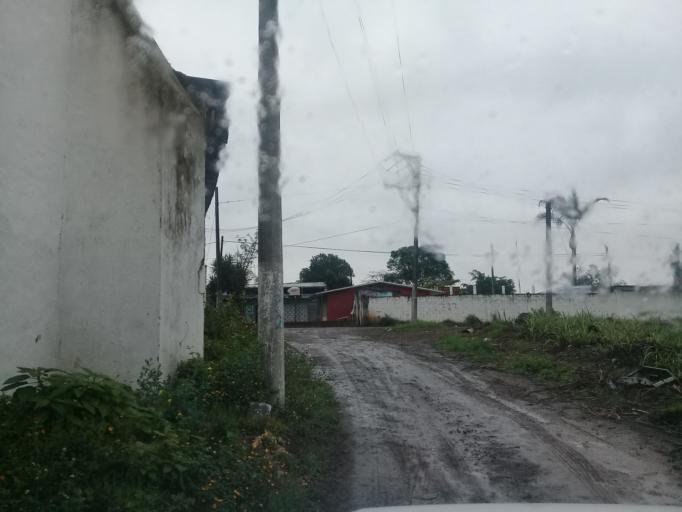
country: MX
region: Veracruz
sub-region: Cordoba
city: San Jose de Tapia
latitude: 18.8469
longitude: -96.9495
